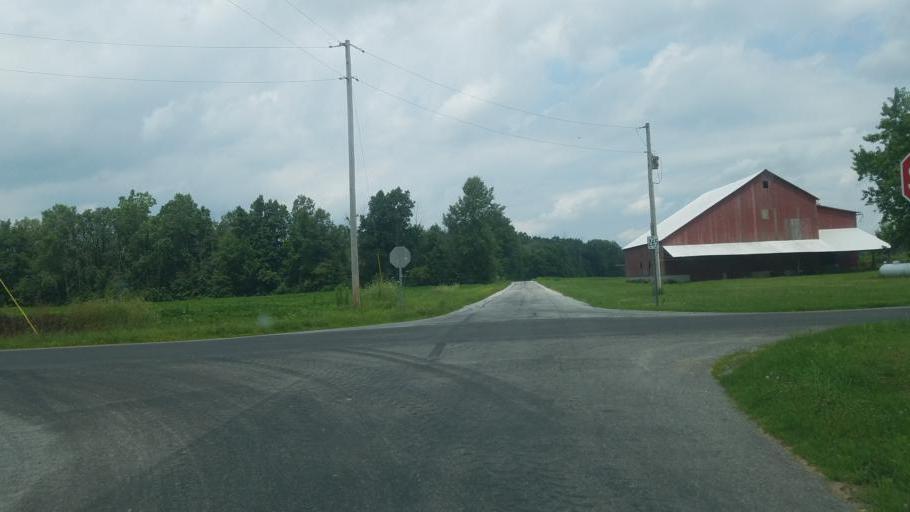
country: US
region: Ohio
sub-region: Hardin County
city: Kenton
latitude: 40.5985
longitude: -83.5413
